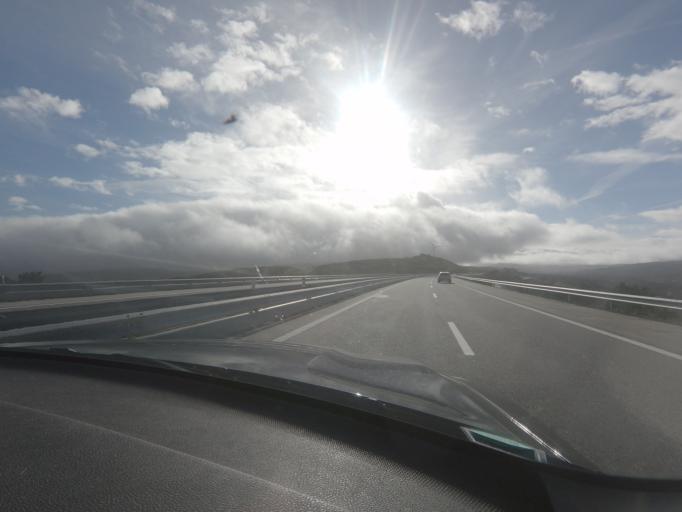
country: PT
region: Viseu
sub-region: Lamego
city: Lamego
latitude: 41.0364
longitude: -7.8620
